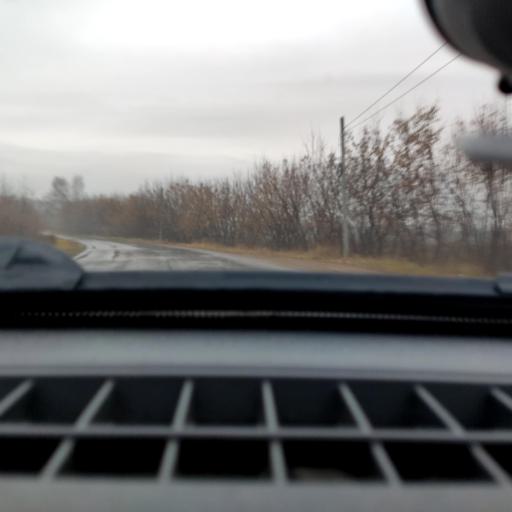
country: RU
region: Bashkortostan
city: Iglino
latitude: 54.8064
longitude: 56.1925
